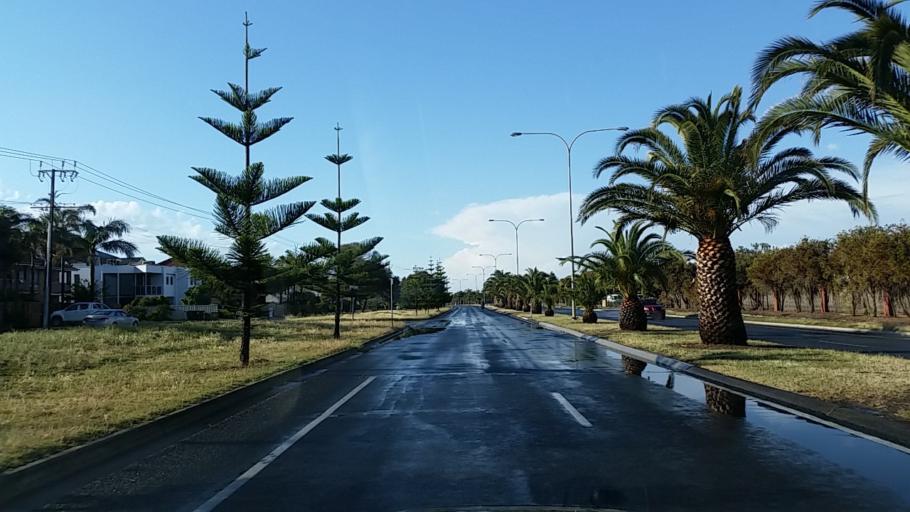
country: AU
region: South Australia
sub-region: Charles Sturt
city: Grange
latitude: -34.8889
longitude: 138.4871
